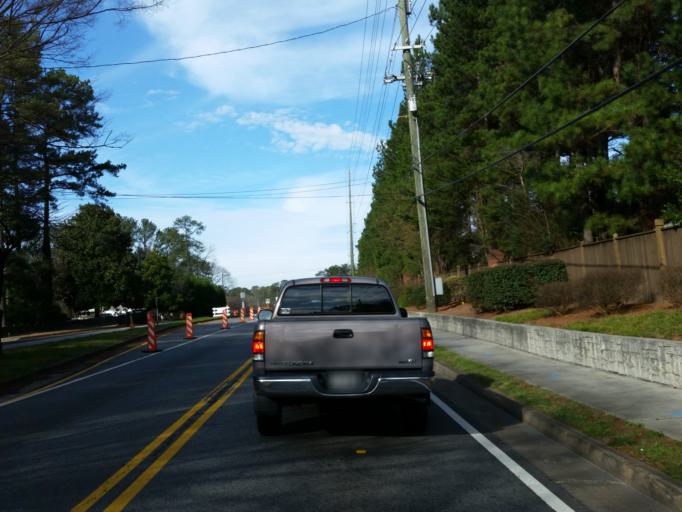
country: US
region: Georgia
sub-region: Cobb County
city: Vinings
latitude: 33.9354
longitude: -84.4609
